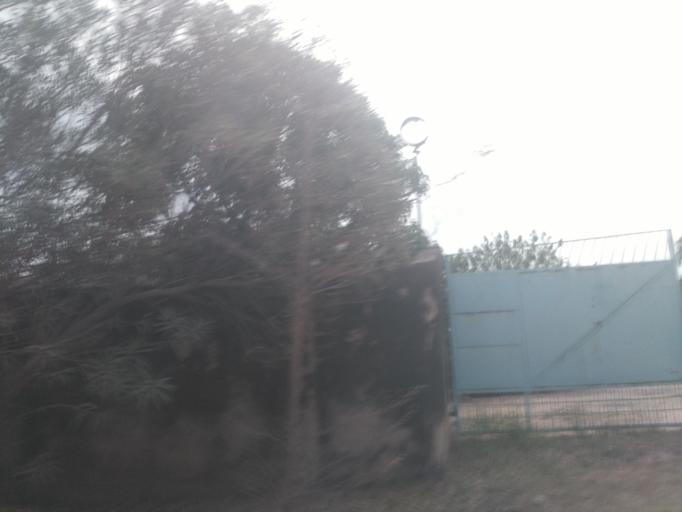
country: TZ
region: Dar es Salaam
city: Magomeni
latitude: -6.7517
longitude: 39.2820
